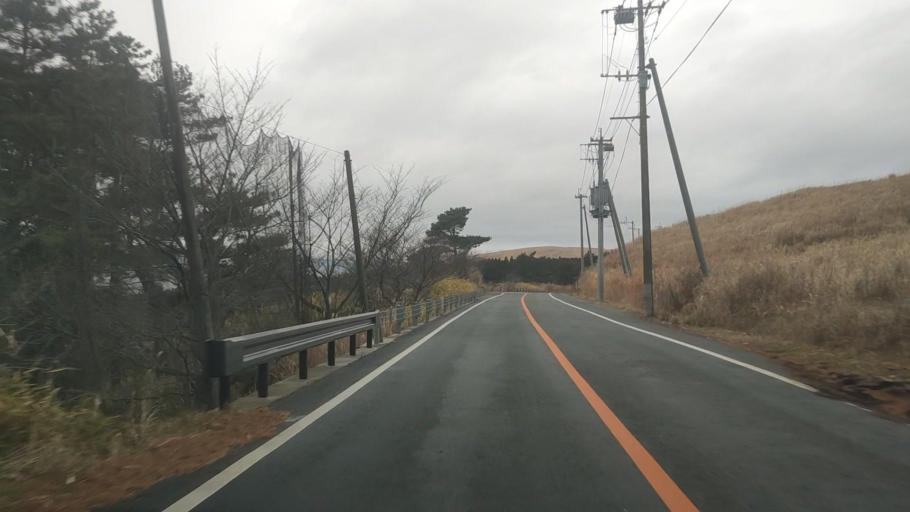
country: JP
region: Kumamoto
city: Aso
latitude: 32.8939
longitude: 131.0271
